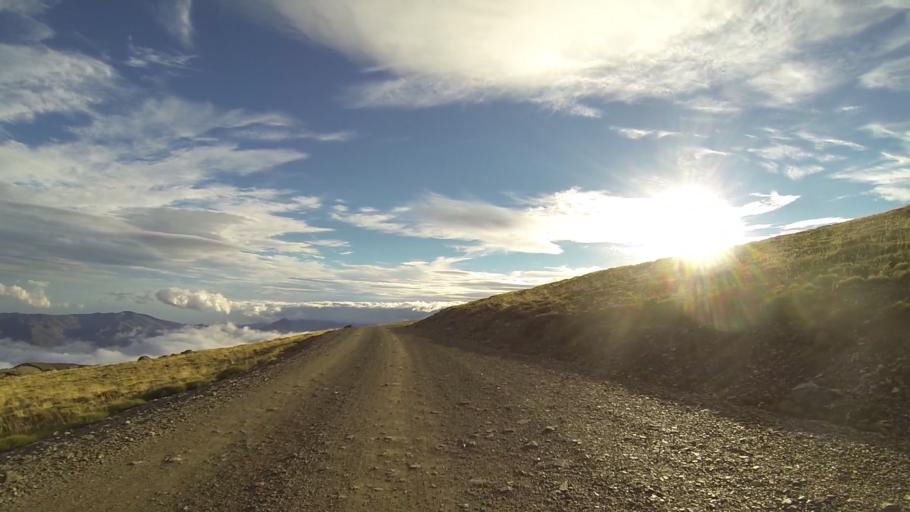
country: ES
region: Andalusia
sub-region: Provincia de Granada
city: Trevelez
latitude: 36.9900
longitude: -3.3113
